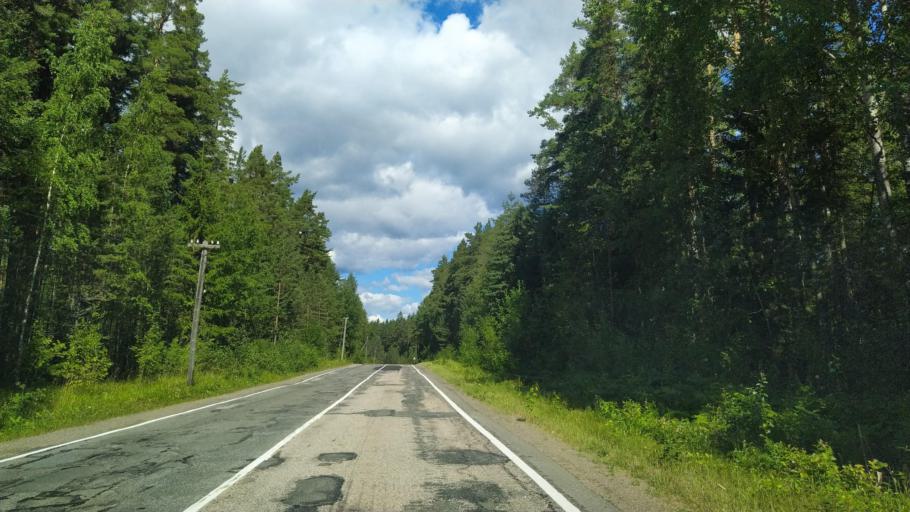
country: RU
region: Leningrad
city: Priozersk
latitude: 60.9853
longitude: 30.2657
